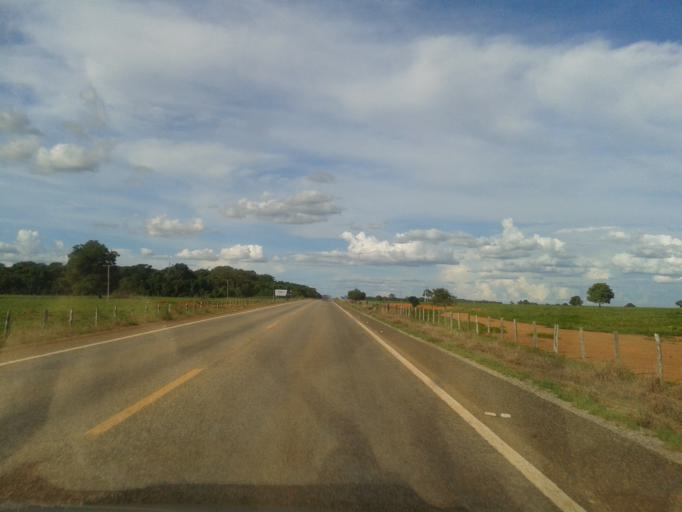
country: BR
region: Goias
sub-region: Mozarlandia
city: Mozarlandia
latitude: -14.3344
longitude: -50.4156
